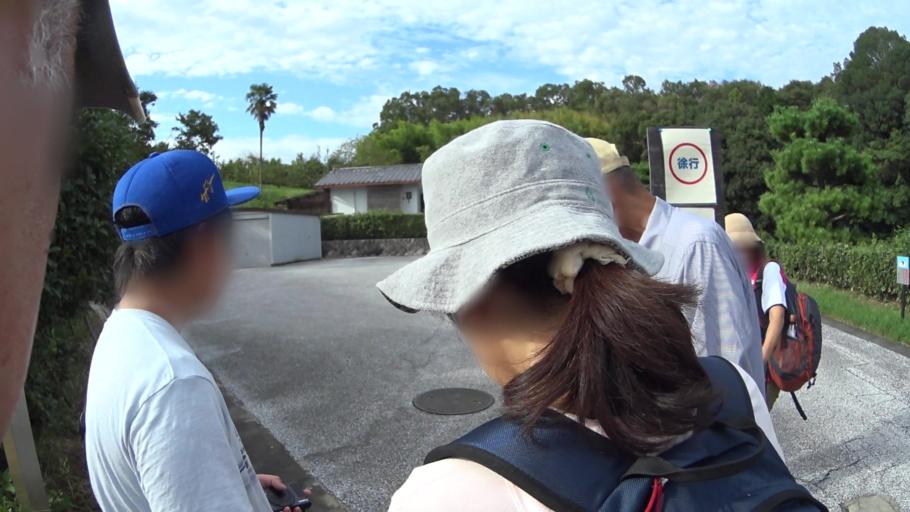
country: JP
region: Nara
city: Kashihara-shi
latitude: 34.4682
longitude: 135.8000
